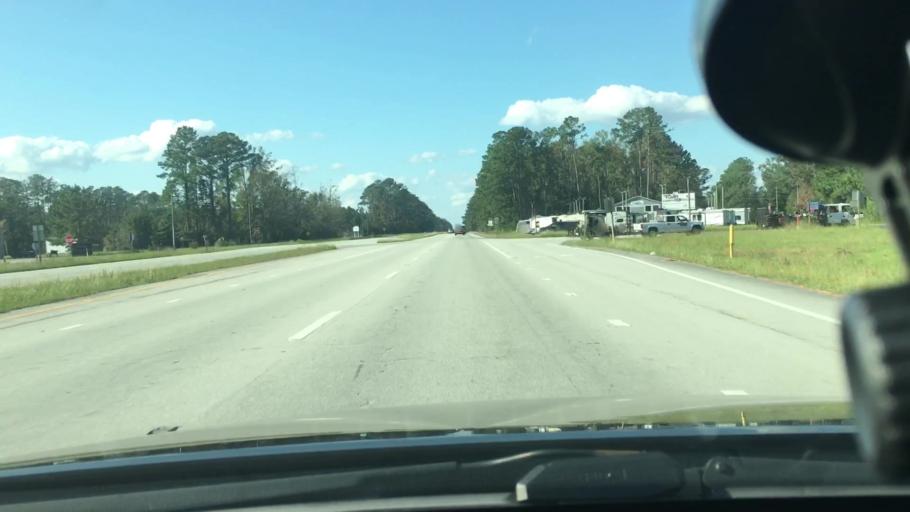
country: US
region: North Carolina
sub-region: Craven County
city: Neuse Forest
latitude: 35.0131
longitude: -76.9935
